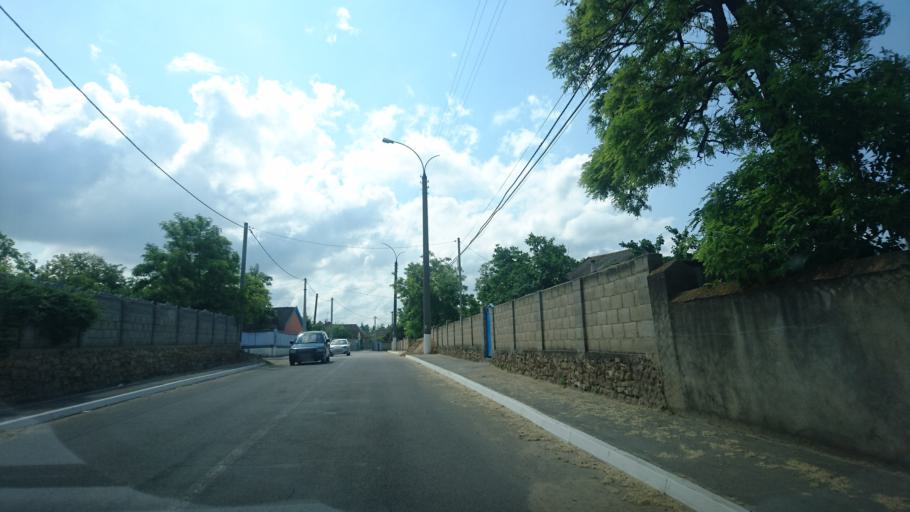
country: MD
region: Telenesti
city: Cocieri
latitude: 47.3496
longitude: 29.1085
